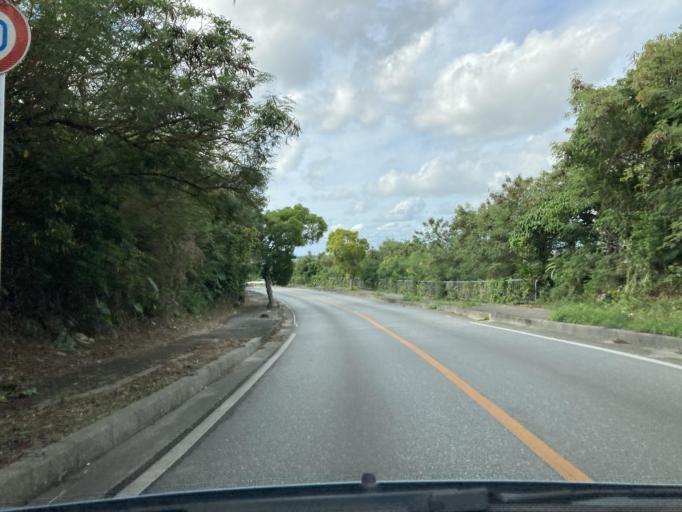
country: JP
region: Okinawa
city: Itoman
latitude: 26.1306
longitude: 127.7097
